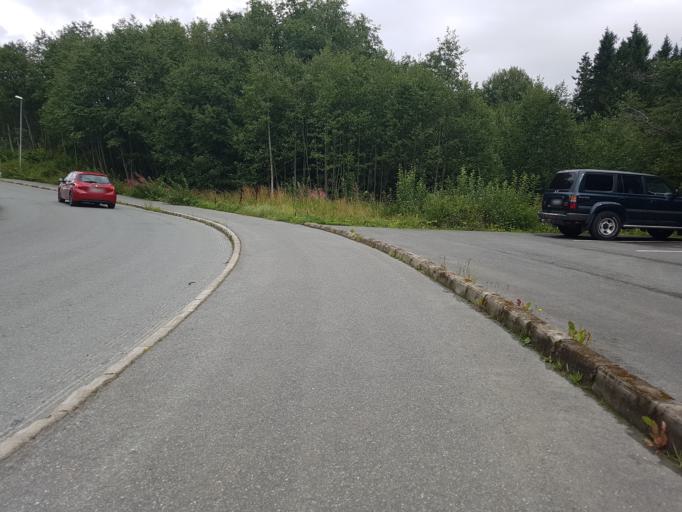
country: NO
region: Sor-Trondelag
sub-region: Trondheim
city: Trondheim
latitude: 63.3856
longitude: 10.3992
